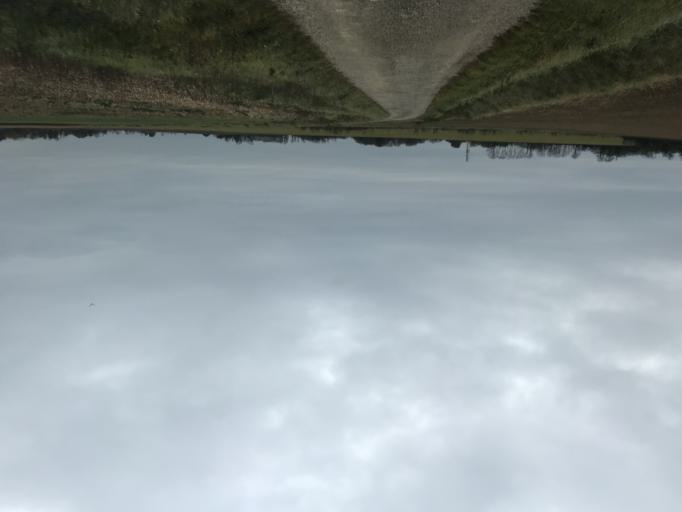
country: FR
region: Rhone-Alpes
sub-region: Departement de l'Ain
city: Miribel
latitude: 45.8408
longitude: 4.9576
